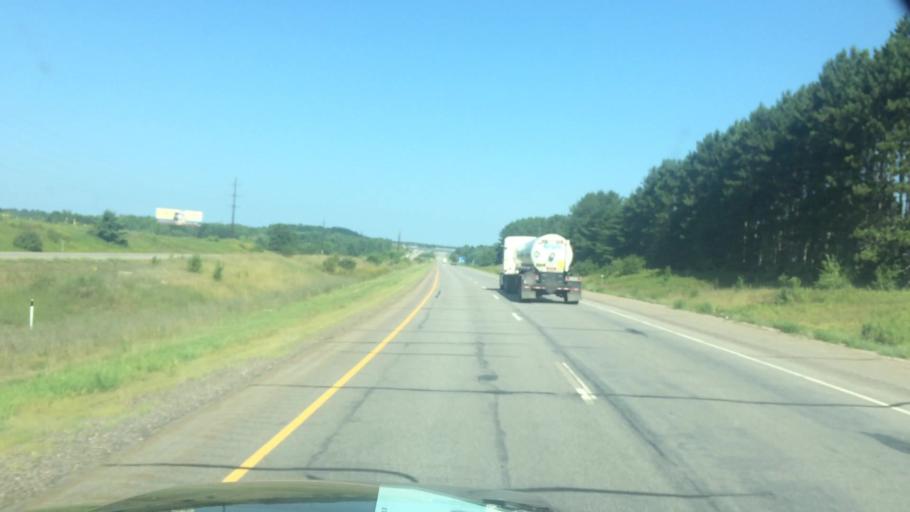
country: US
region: Wisconsin
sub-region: Lincoln County
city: Merrill
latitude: 45.1983
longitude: -89.6500
